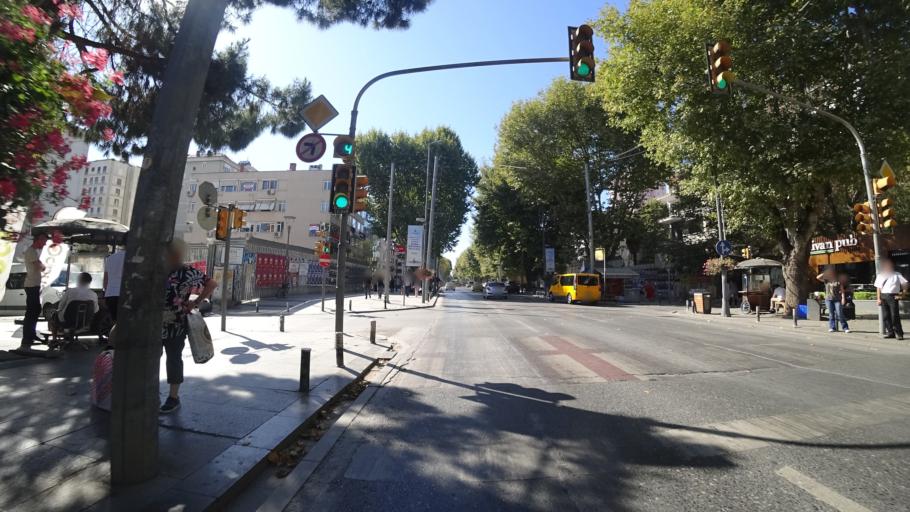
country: TR
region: Istanbul
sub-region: Atasehir
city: Atasehir
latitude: 40.9647
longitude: 29.0725
